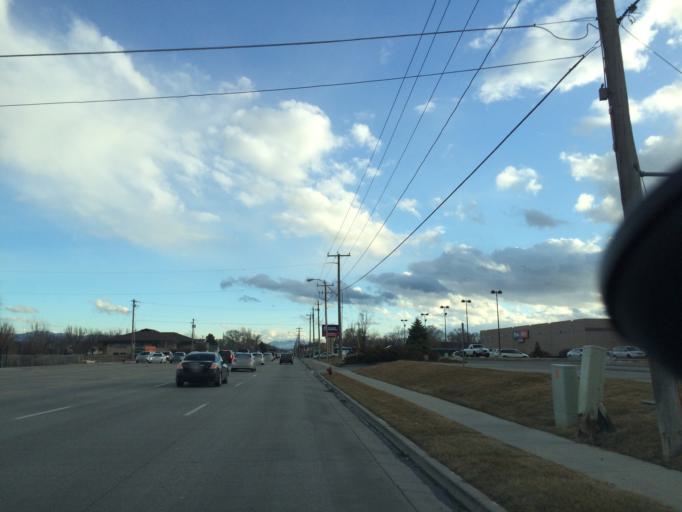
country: US
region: Utah
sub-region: Salt Lake County
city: West Jordan
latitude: 40.6220
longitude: -111.9389
